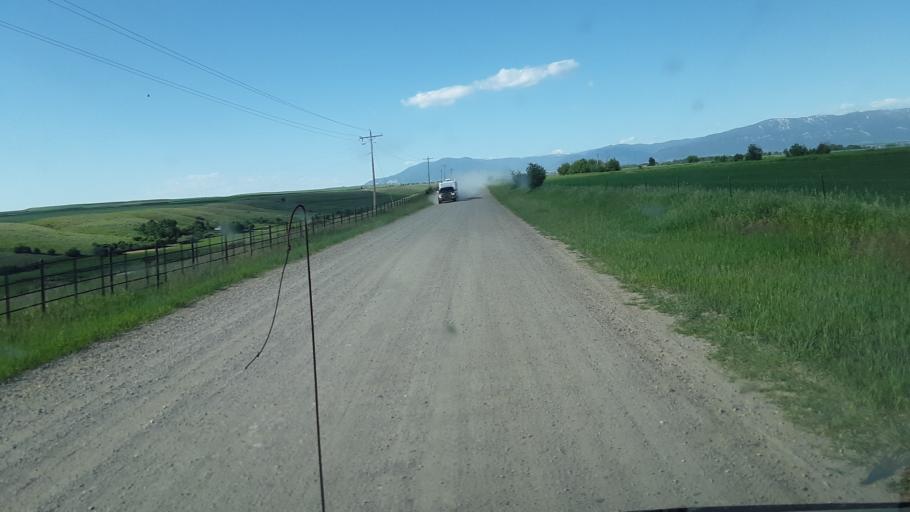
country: US
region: Montana
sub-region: Carbon County
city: Red Lodge
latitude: 45.3465
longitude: -109.1560
